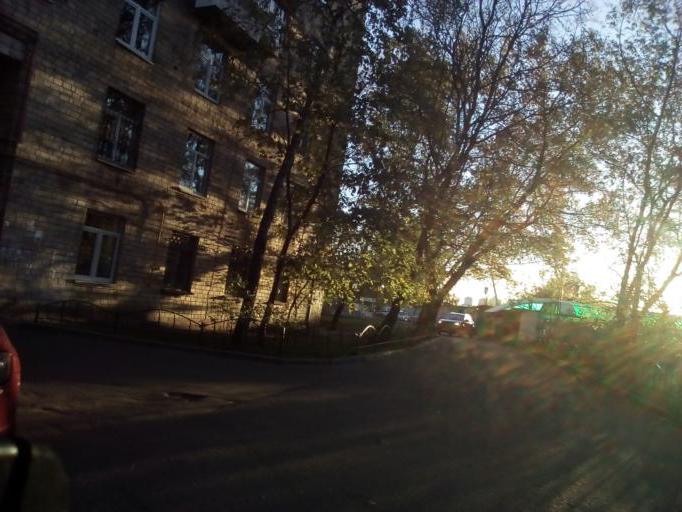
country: RU
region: Moskovskaya
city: Koptevo
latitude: 55.8233
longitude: 37.4926
